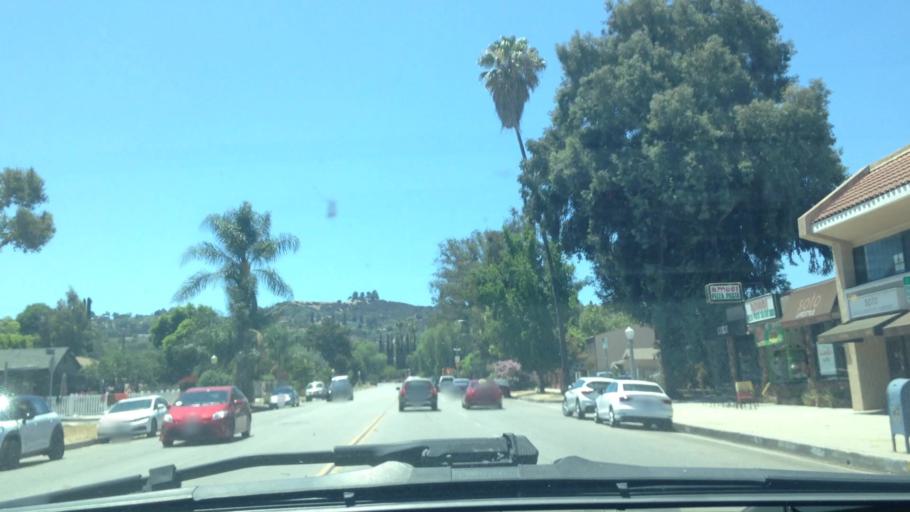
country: US
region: California
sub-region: Los Angeles County
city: Woodland Hills
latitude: 34.1565
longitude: -118.6058
